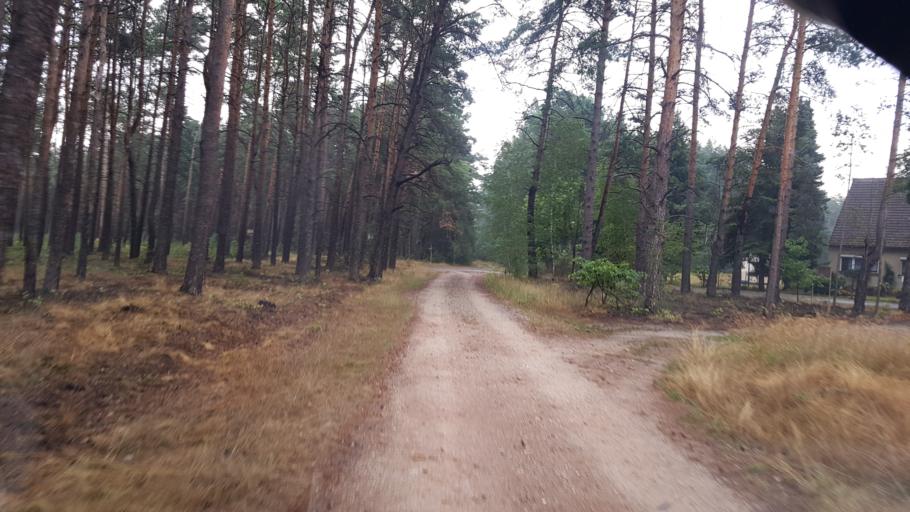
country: DE
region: Brandenburg
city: Finsterwalde
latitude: 51.6456
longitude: 13.7844
